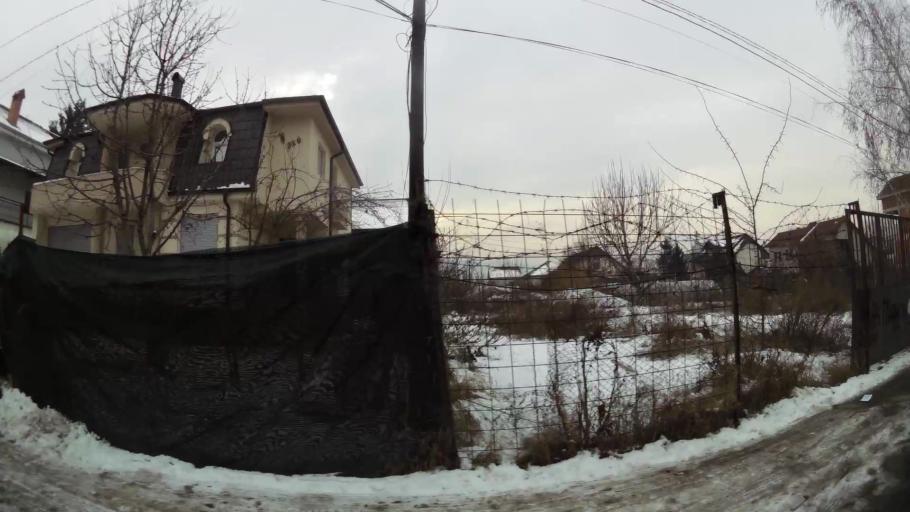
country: MK
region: Butel
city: Butel
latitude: 42.0383
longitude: 21.4490
